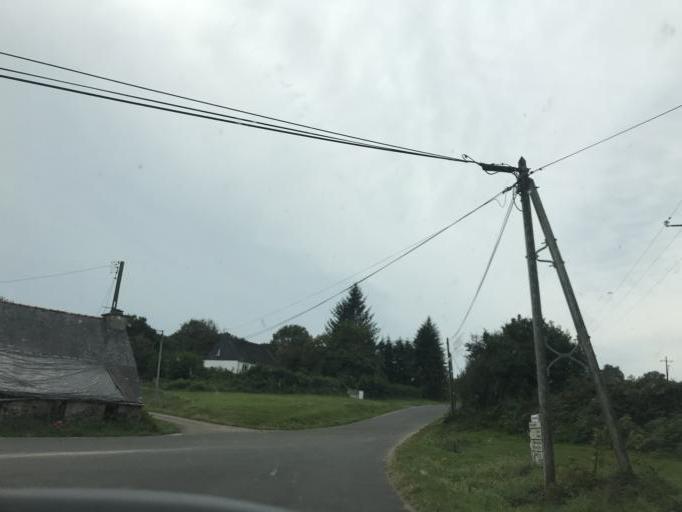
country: FR
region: Brittany
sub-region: Departement du Finistere
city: Plouneour-Menez
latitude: 48.3652
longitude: -3.8595
